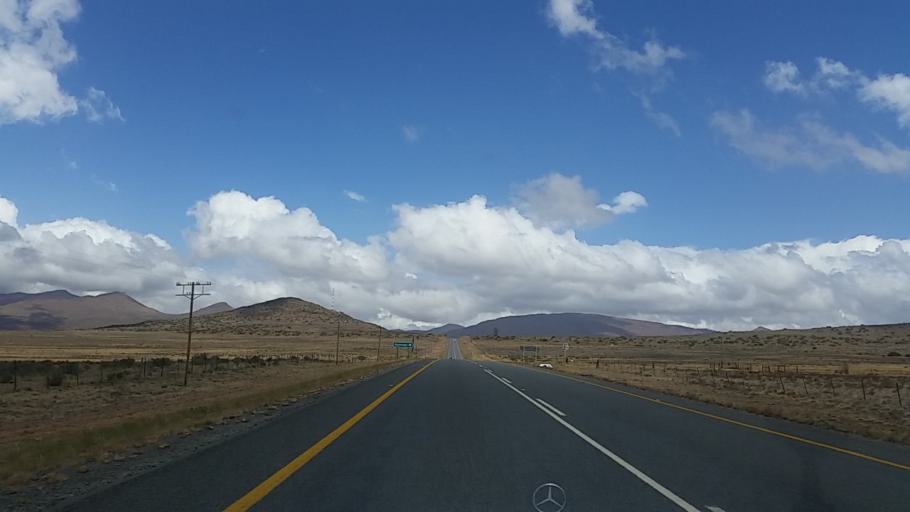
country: ZA
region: Eastern Cape
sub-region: Chris Hani District Municipality
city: Middelburg
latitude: -31.7622
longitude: 24.9205
